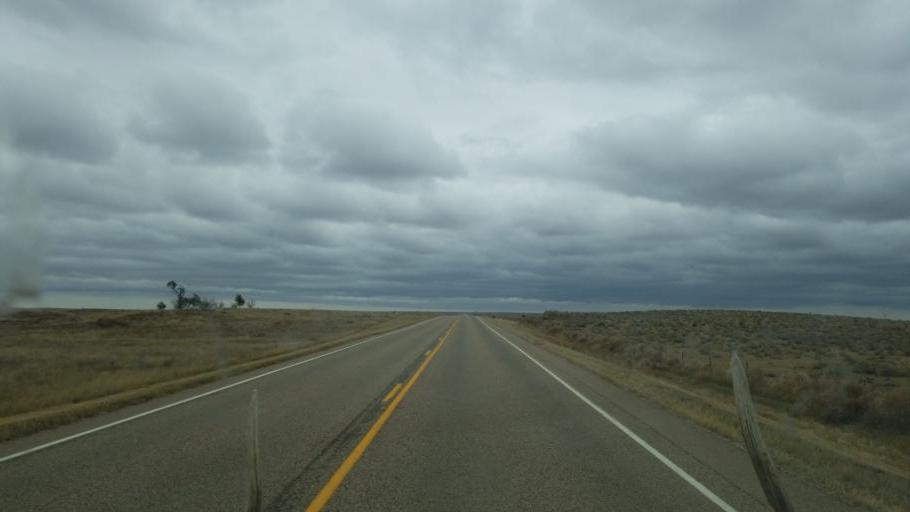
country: US
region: Colorado
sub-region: Kiowa County
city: Eads
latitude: 38.7851
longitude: -102.6983
